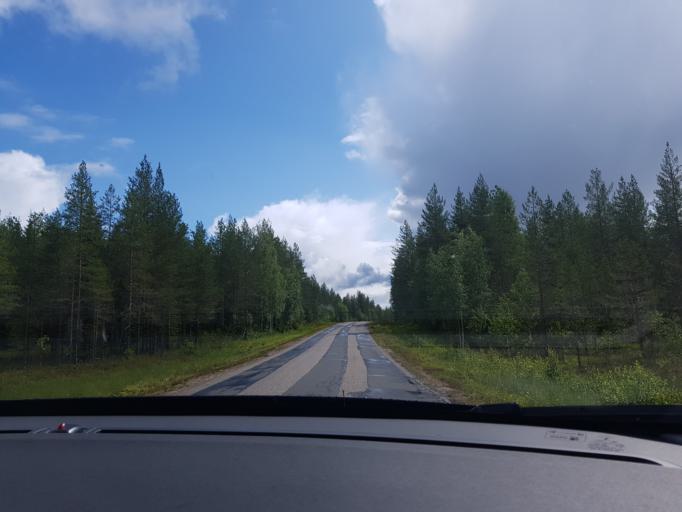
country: FI
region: Kainuu
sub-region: Kehys-Kainuu
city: Kuhmo
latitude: 64.4599
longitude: 29.6346
